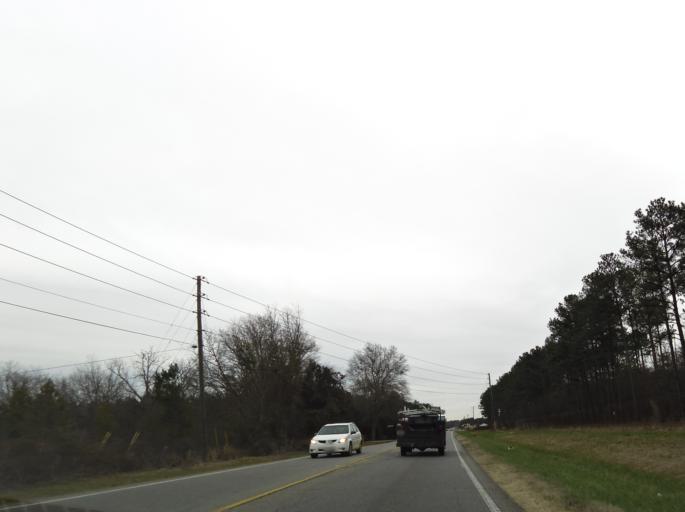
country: US
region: Georgia
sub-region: Peach County
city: Byron
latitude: 32.6721
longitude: -83.7253
